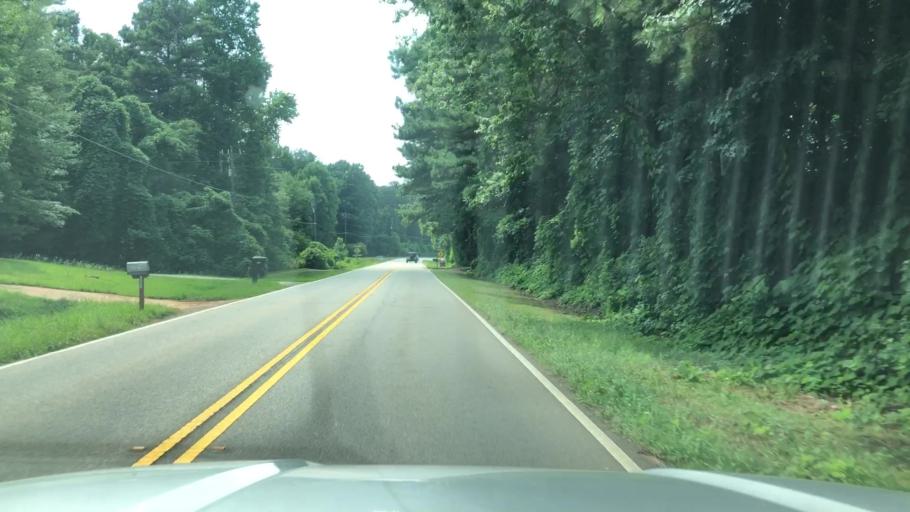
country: US
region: Georgia
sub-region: Paulding County
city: Hiram
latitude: 33.9390
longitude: -84.7597
